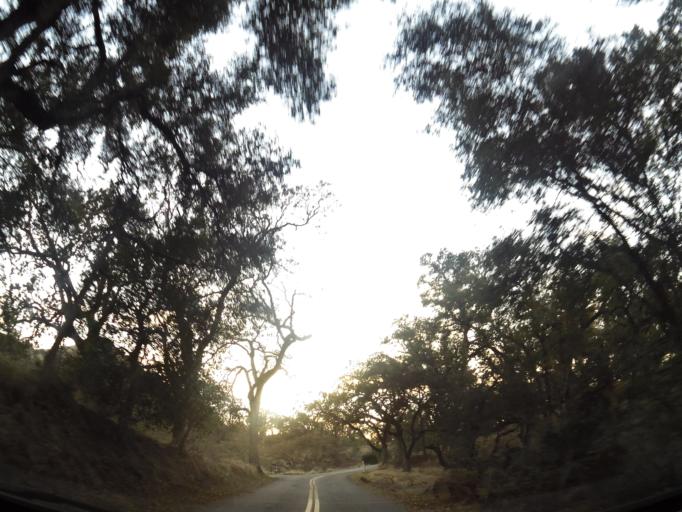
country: US
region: California
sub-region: San Benito County
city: San Juan Bautista
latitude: 36.7607
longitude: -121.5007
